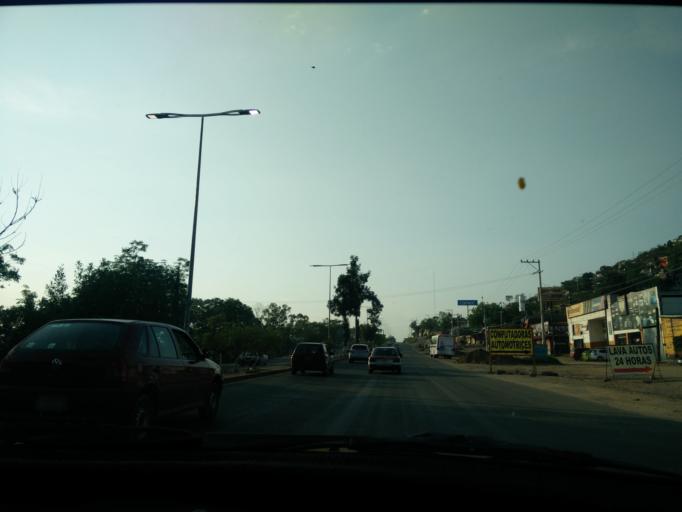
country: MX
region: Oaxaca
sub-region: Santa Maria Atzompa
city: San Jeronimo Yahuiche
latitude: 17.1053
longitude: -96.7533
